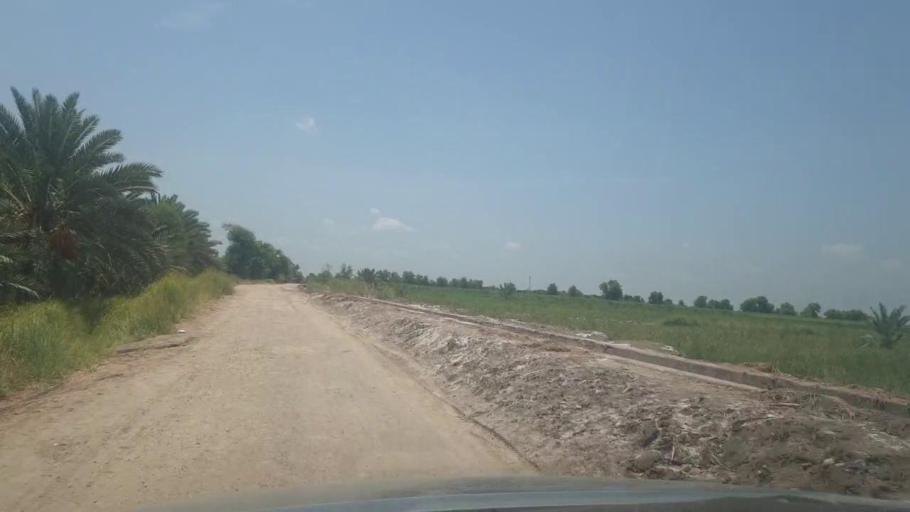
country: PK
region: Sindh
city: Kot Diji
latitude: 27.3880
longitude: 68.6940
